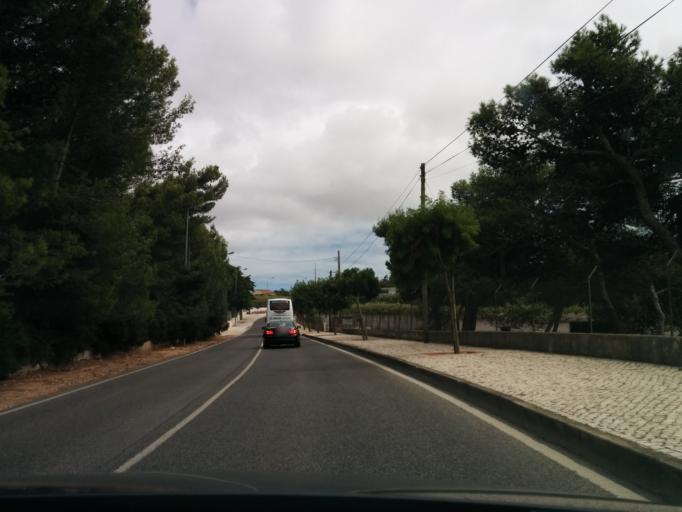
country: PT
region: Lisbon
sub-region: Cascais
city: Alcabideche
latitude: 38.7330
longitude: -9.4470
